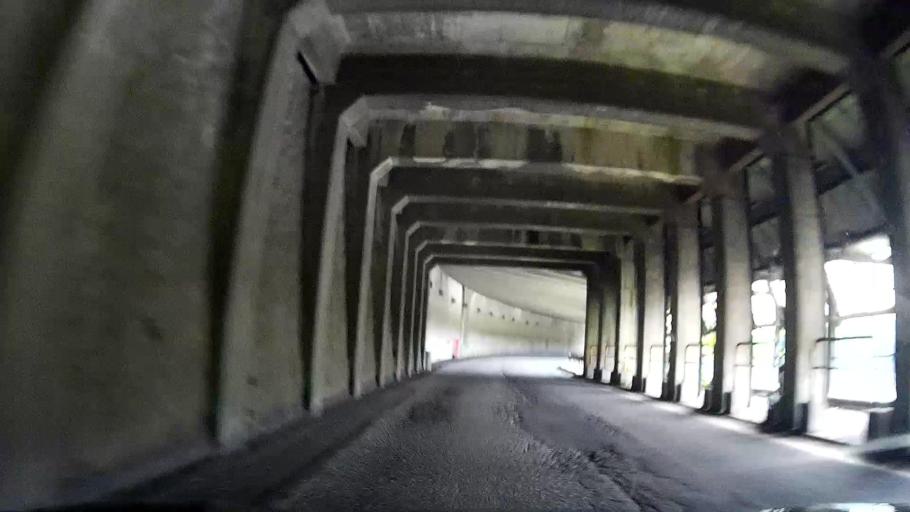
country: JP
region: Niigata
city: Tokamachi
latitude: 36.9967
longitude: 138.6162
